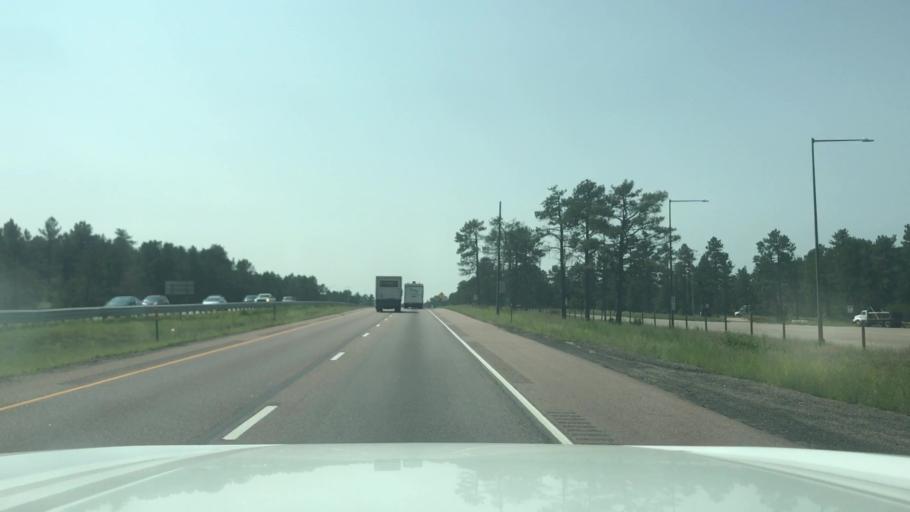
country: US
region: Colorado
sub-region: El Paso County
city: Palmer Lake
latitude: 39.2301
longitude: -104.8779
